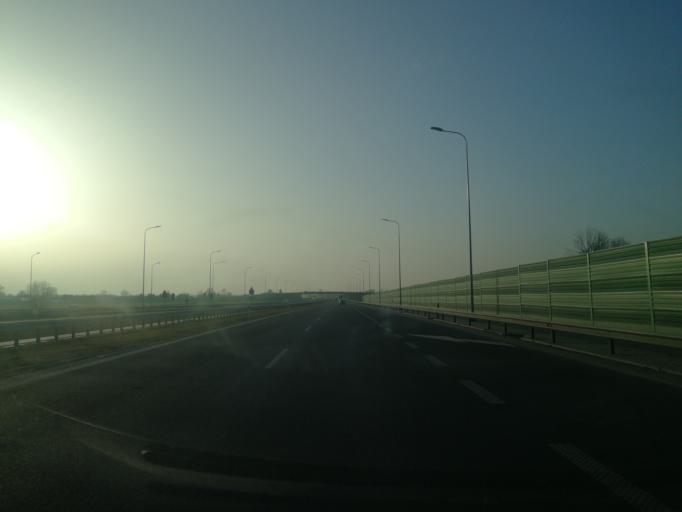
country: PL
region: Warmian-Masurian Voivodeship
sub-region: Powiat elblaski
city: Elblag
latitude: 54.1643
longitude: 19.3408
